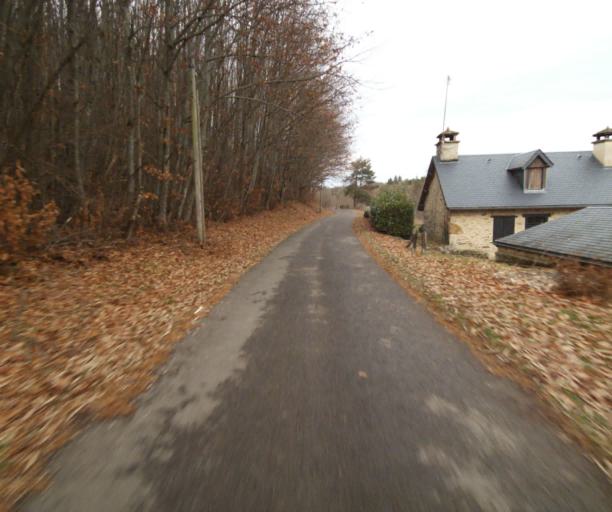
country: FR
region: Limousin
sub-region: Departement de la Correze
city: Chameyrat
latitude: 45.2329
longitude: 1.6878
